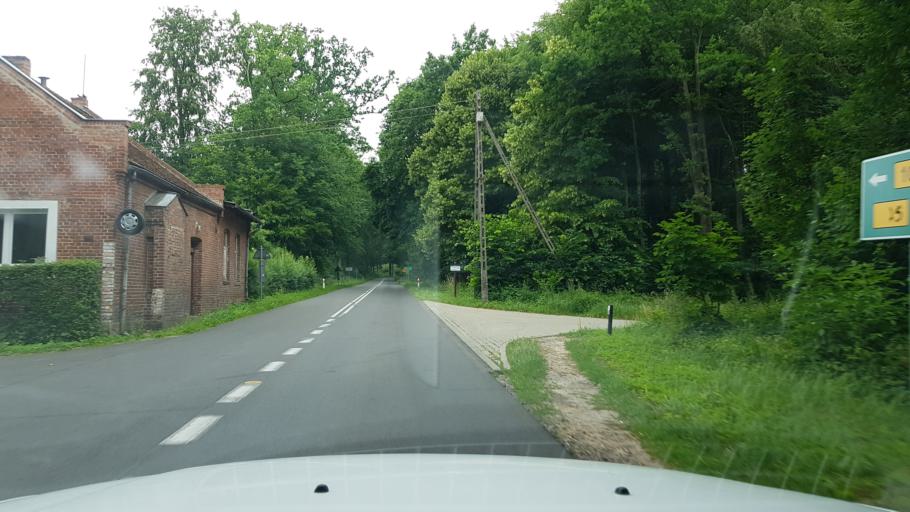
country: PL
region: West Pomeranian Voivodeship
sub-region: Powiat gryficki
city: Gryfice
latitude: 53.9062
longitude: 15.1389
